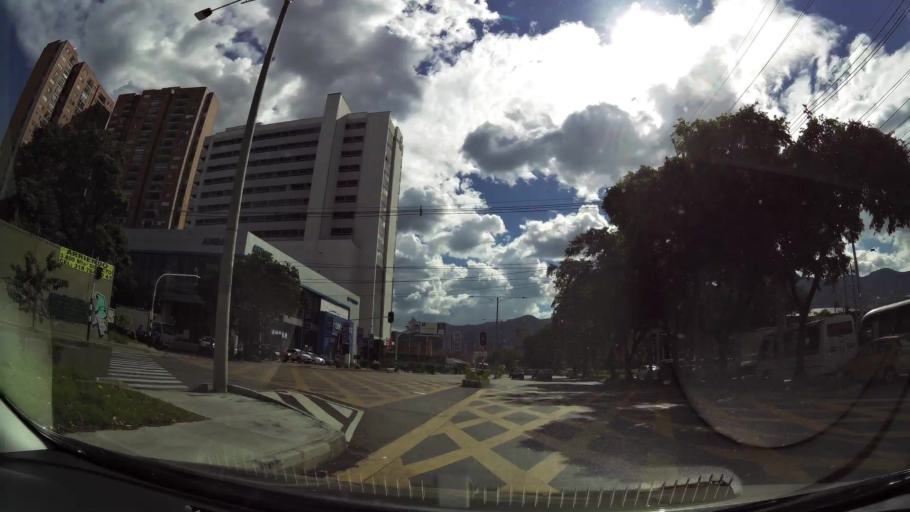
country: CO
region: Antioquia
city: Sabaneta
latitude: 6.1579
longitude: -75.6093
